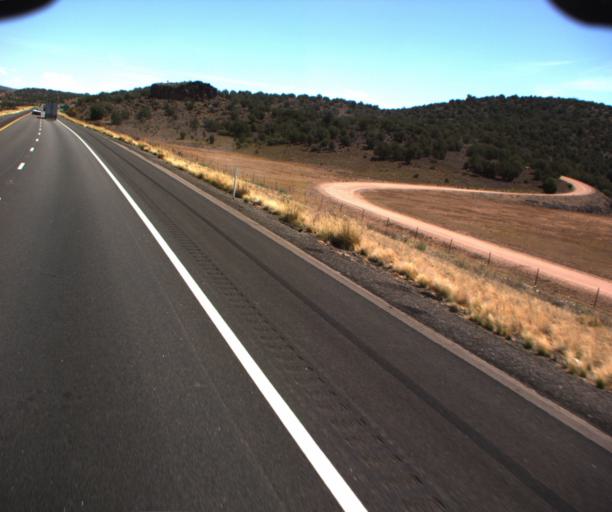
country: US
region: Arizona
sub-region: Mohave County
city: Peach Springs
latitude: 35.1842
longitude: -113.4501
